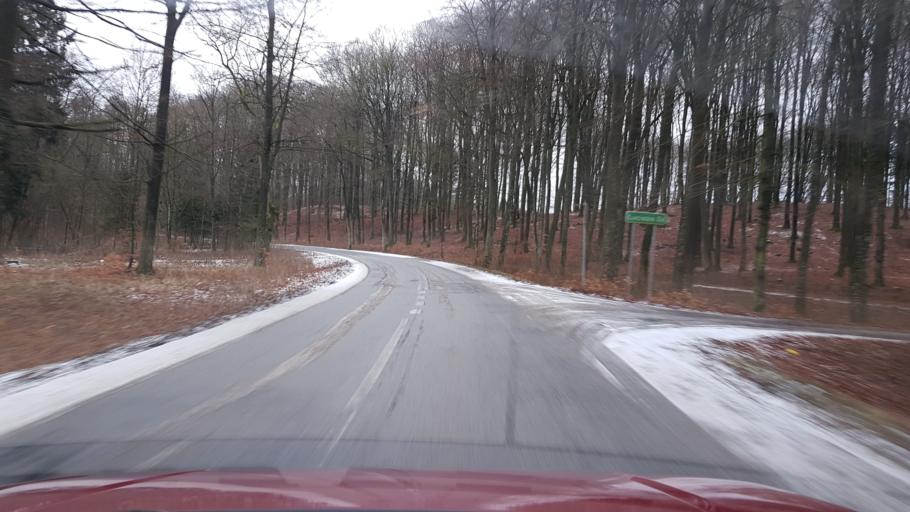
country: PL
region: West Pomeranian Voivodeship
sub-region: Powiat lobeski
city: Resko
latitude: 53.8400
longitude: 15.3736
